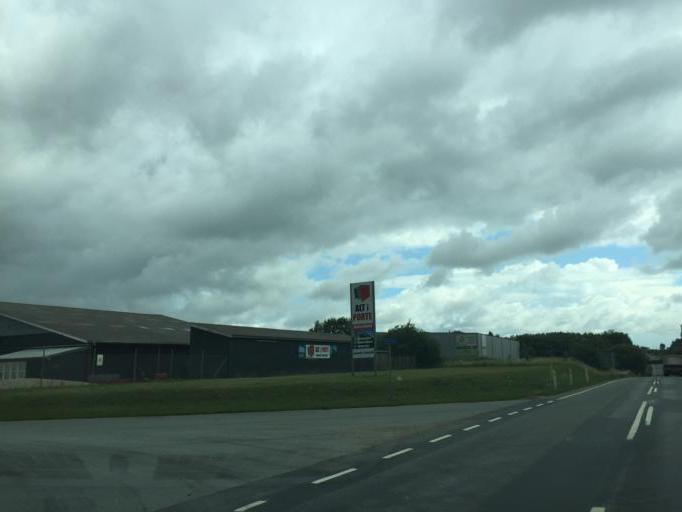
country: DK
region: South Denmark
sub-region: Faaborg-Midtfyn Kommune
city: Arslev
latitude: 55.3043
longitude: 10.4539
